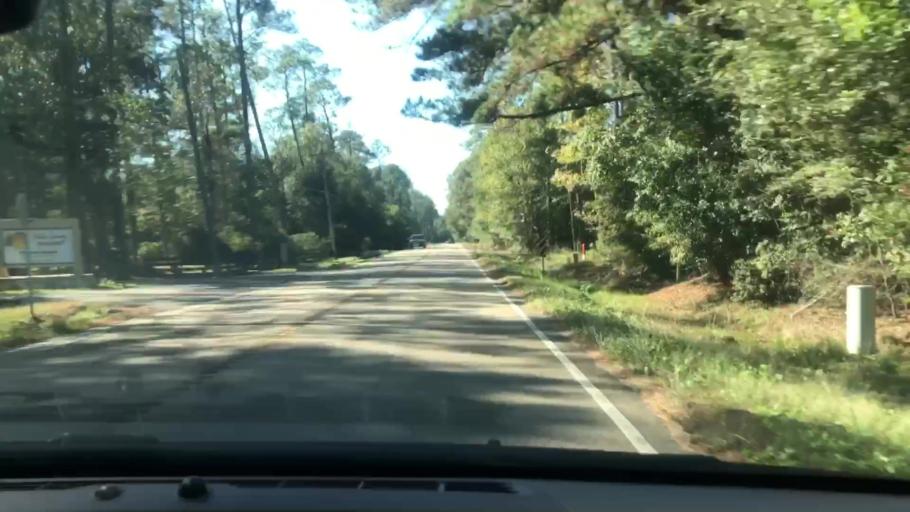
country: US
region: Louisiana
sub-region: Saint Tammany Parish
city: Abita Springs
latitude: 30.4964
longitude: -90.0044
